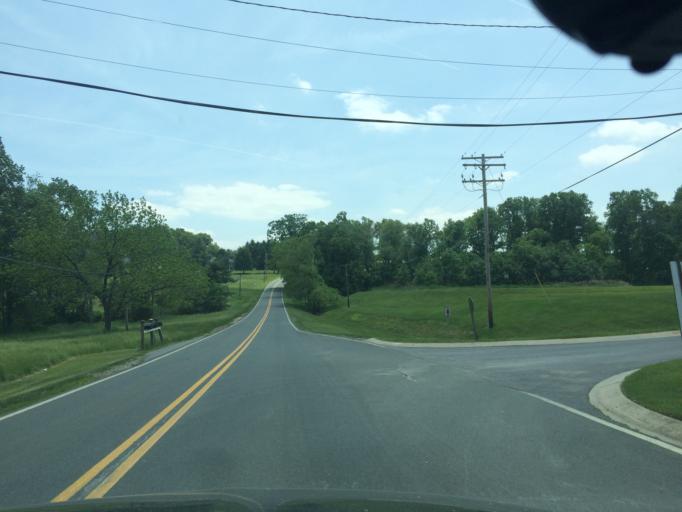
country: US
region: Maryland
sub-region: Carroll County
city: Eldersburg
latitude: 39.4320
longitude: -76.9923
